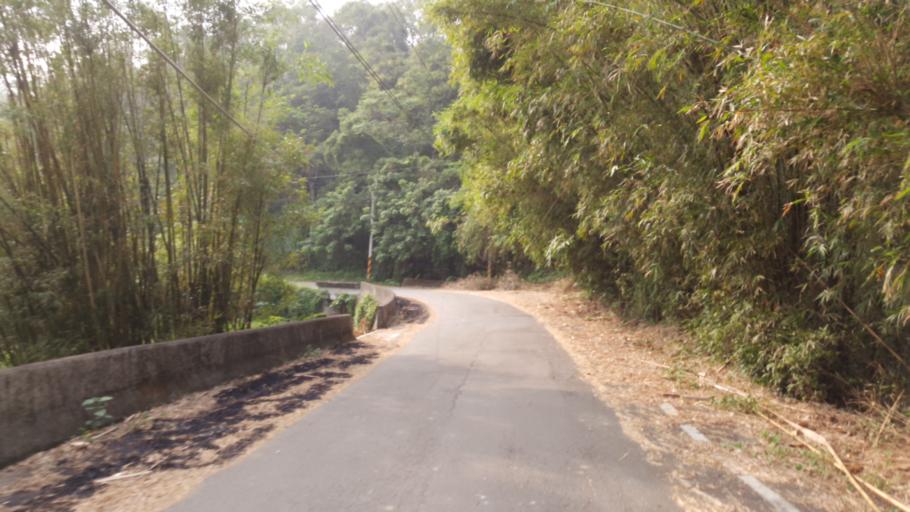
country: TW
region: Taiwan
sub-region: Hsinchu
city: Hsinchu
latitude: 24.7211
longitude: 120.9551
